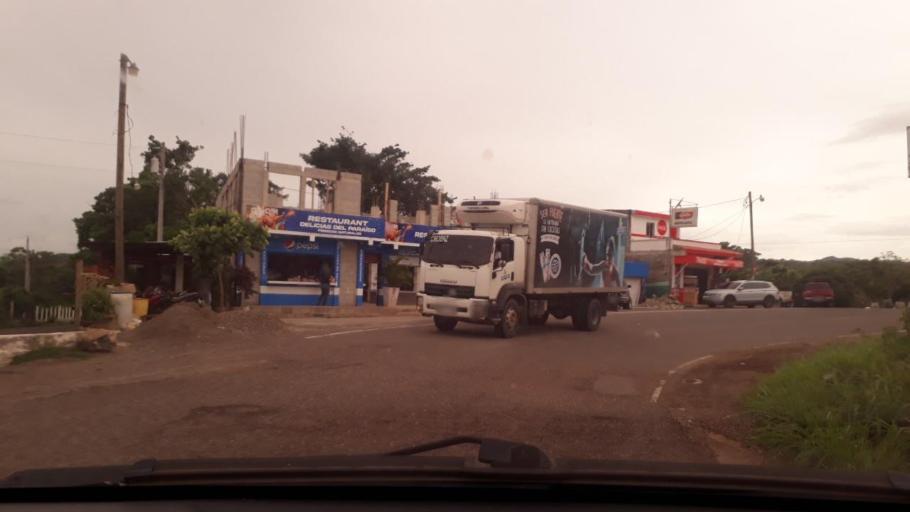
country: GT
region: Jutiapa
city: Asuncion Mita
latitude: 14.3701
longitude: -89.7348
